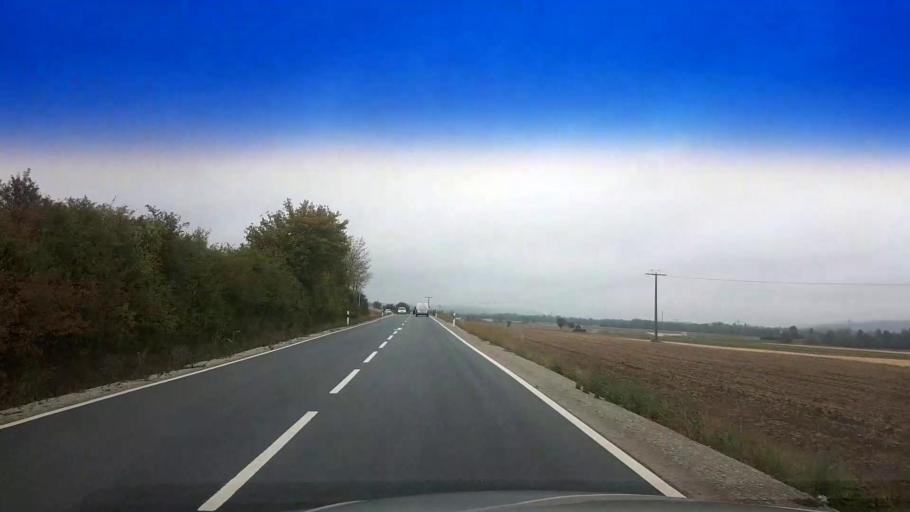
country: DE
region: Bavaria
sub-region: Upper Franconia
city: Buttenheim
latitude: 49.7903
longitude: 11.0391
